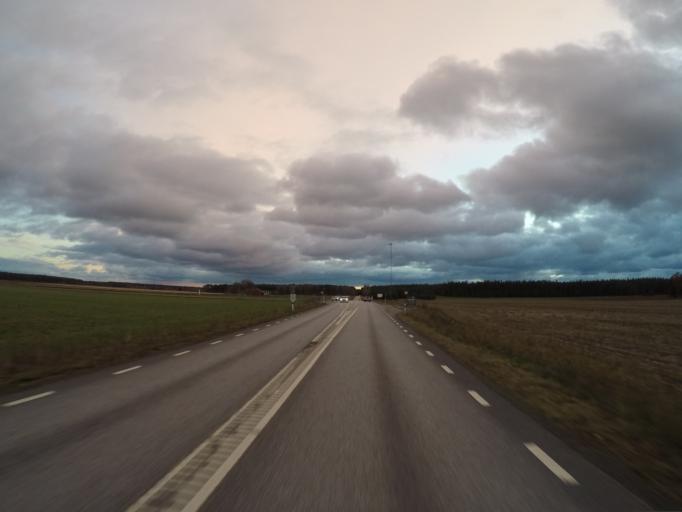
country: SE
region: Skane
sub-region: Kristianstads Kommun
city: Degeberga
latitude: 55.9252
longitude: 14.0741
